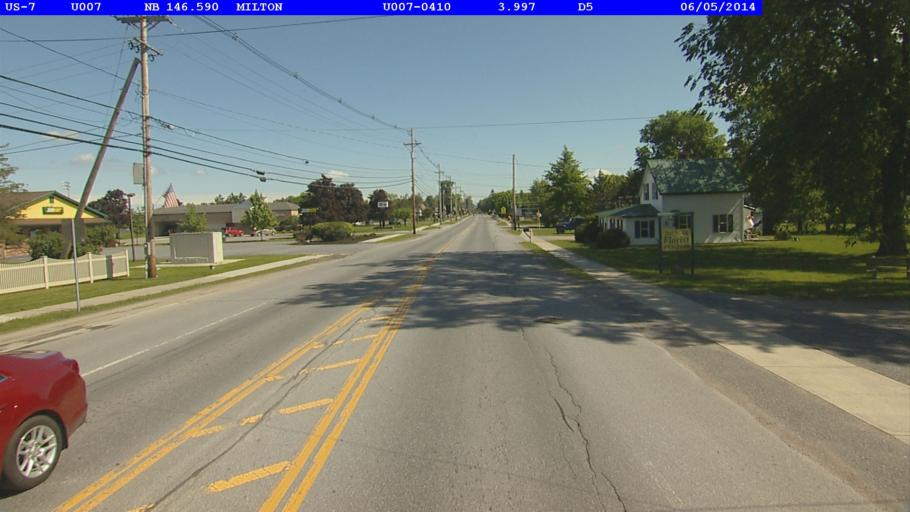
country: US
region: Vermont
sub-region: Chittenden County
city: Milton
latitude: 44.6253
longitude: -73.1177
